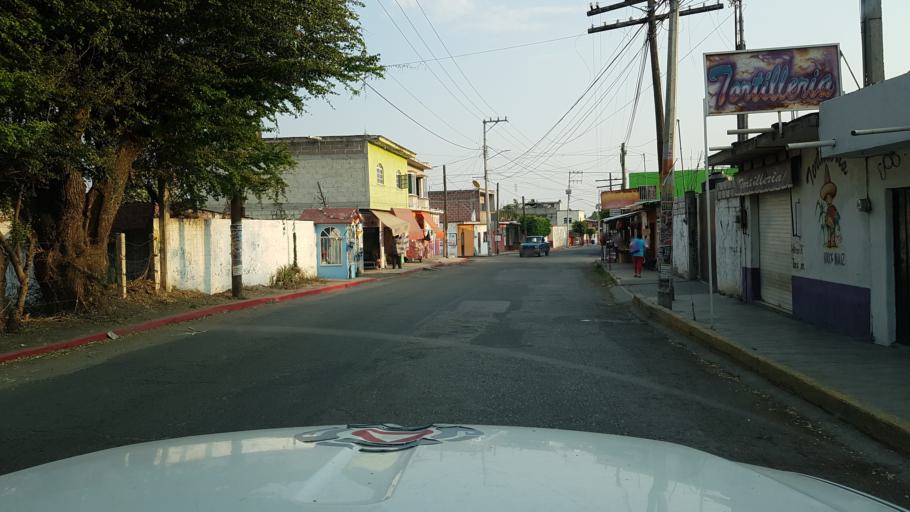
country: MX
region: Morelos
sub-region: Ayala
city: Ciudad Ayala
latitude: 18.7826
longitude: -98.9800
